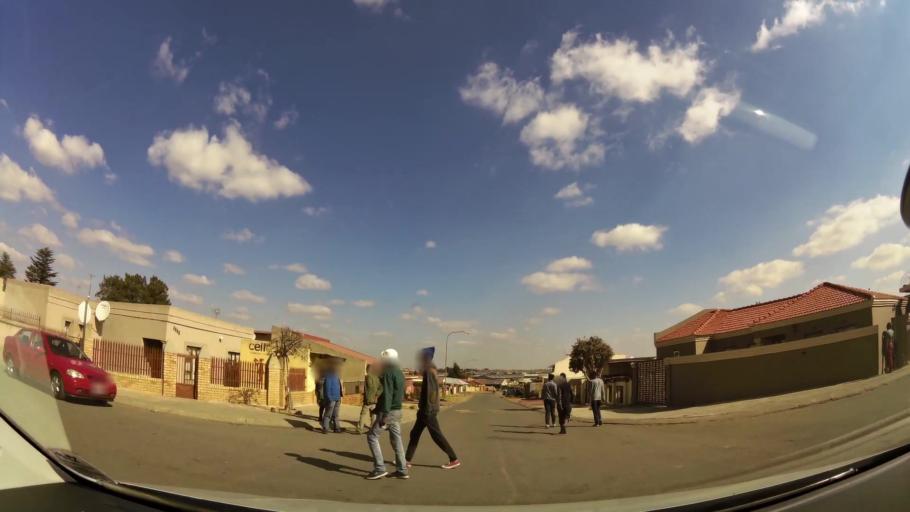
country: ZA
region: Gauteng
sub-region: City of Johannesburg Metropolitan Municipality
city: Roodepoort
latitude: -26.2099
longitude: 27.8821
